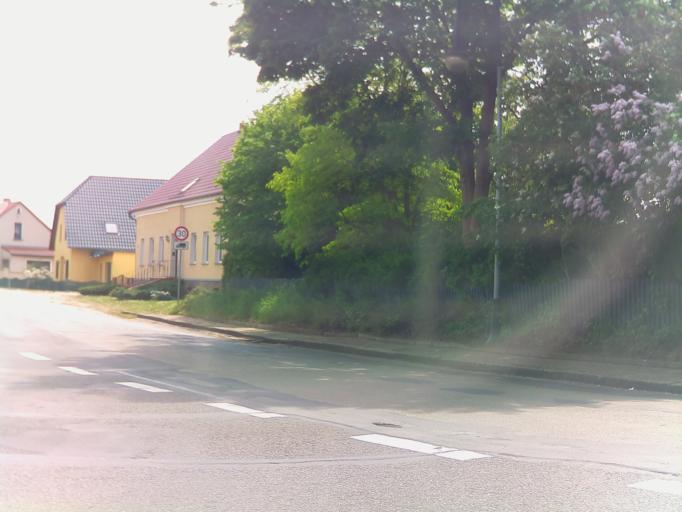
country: DE
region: Brandenburg
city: Nennhausen
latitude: 52.6056
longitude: 12.5075
